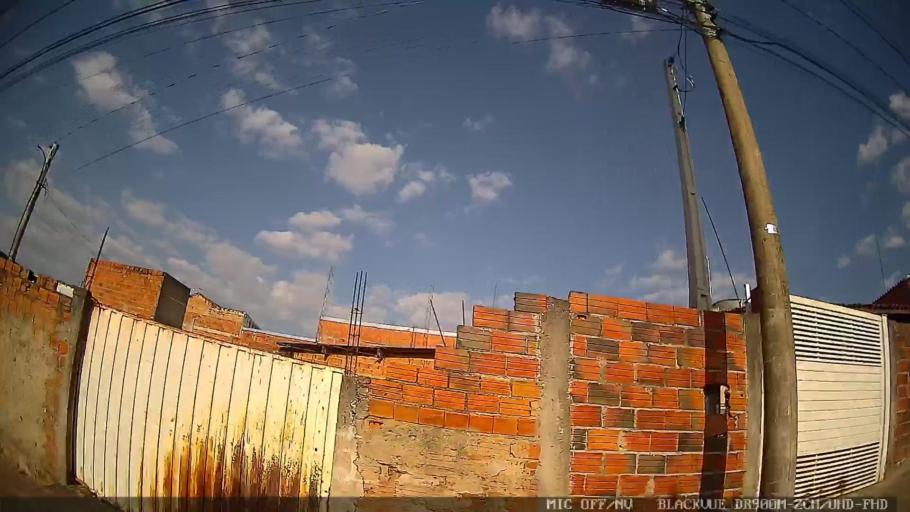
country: BR
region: Sao Paulo
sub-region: Cabreuva
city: Cabreuva
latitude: -23.2648
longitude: -47.0643
